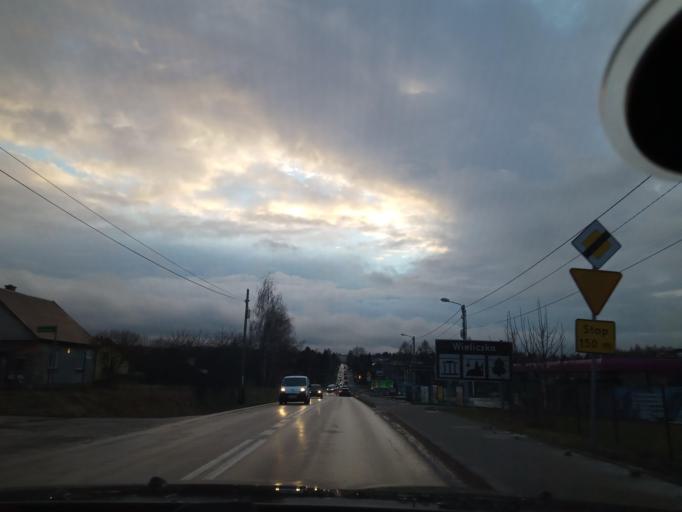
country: PL
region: Lesser Poland Voivodeship
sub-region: Powiat wielicki
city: Wieliczka
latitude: 49.9908
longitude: 20.0829
